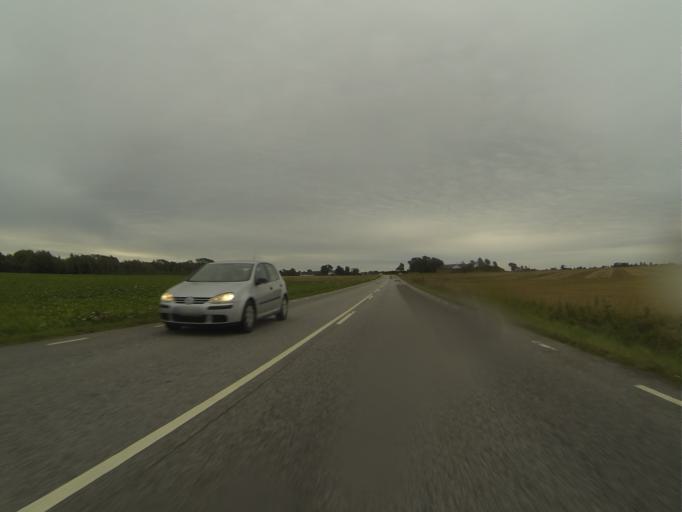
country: SE
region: Skane
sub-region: Svedala Kommun
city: Klagerup
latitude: 55.6357
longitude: 13.2825
